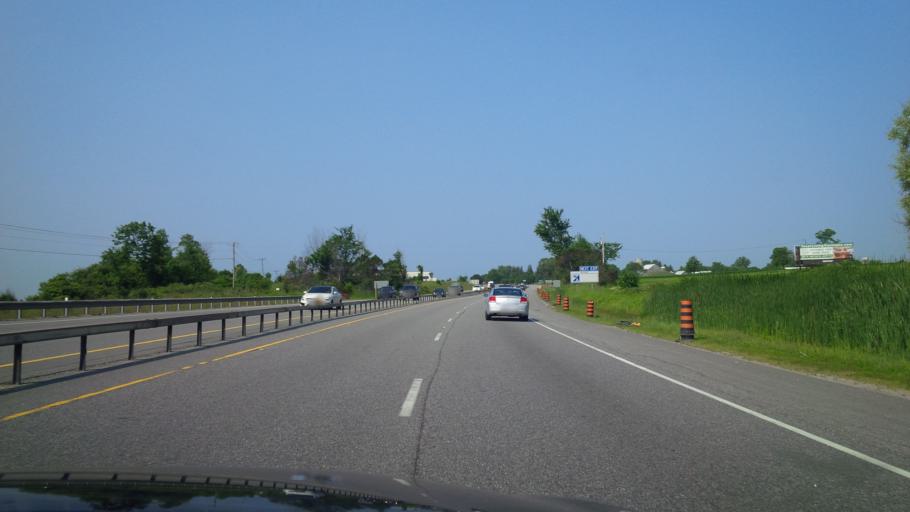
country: CA
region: Ontario
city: Barrie
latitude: 44.4384
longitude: -79.6327
